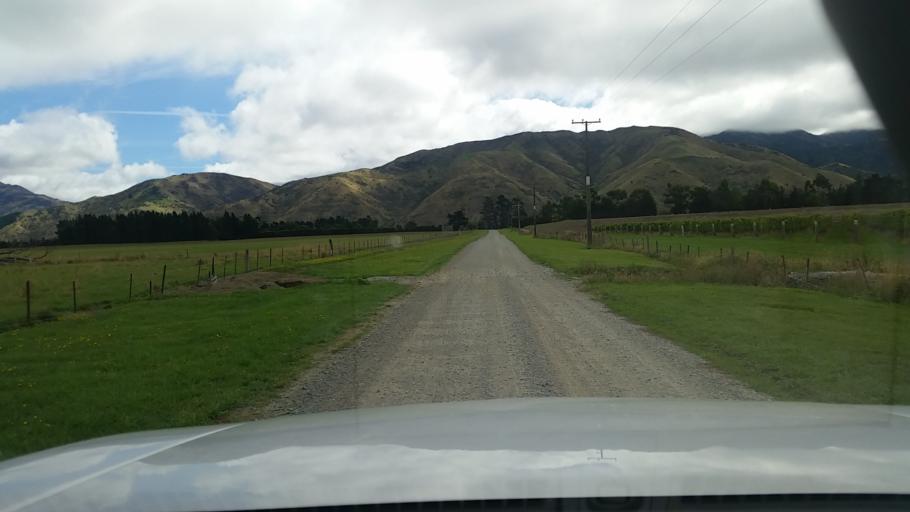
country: NZ
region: Marlborough
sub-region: Marlborough District
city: Blenheim
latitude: -41.6993
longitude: 173.9539
